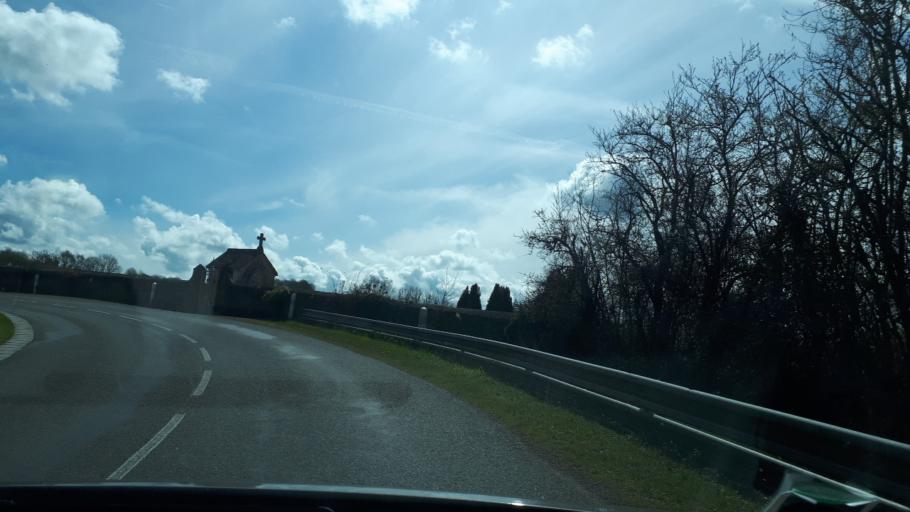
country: FR
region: Pays de la Loire
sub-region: Departement de la Sarthe
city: Bouloire
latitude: 47.9012
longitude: 0.5775
